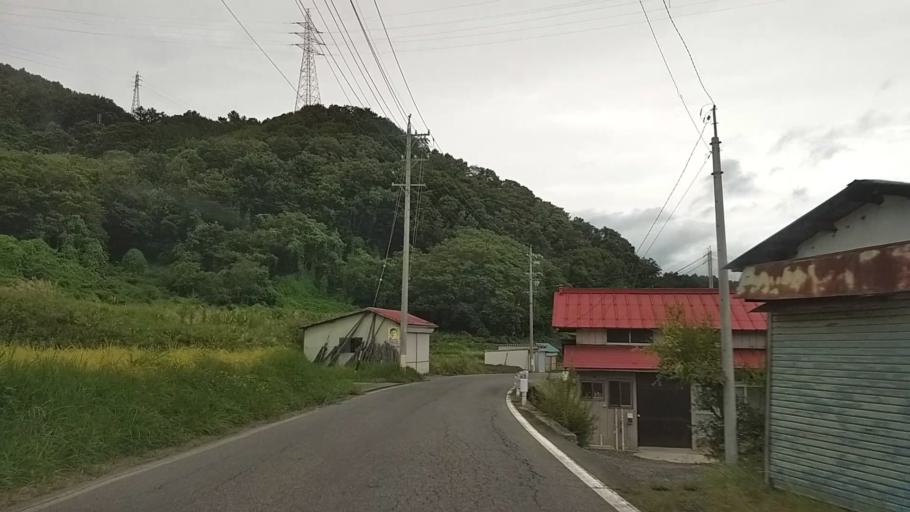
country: JP
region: Nagano
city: Nakano
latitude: 36.7974
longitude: 138.3441
